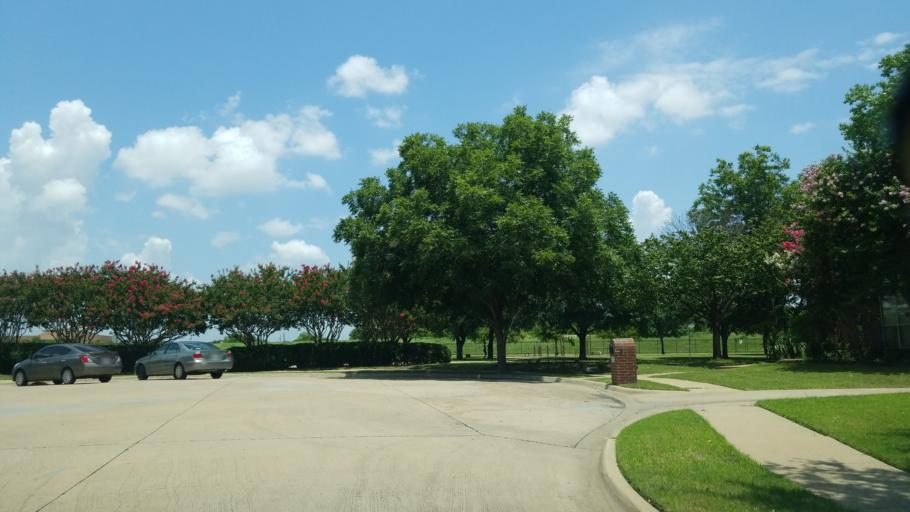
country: US
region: Texas
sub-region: Dallas County
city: Farmers Branch
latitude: 32.9475
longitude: -96.9523
